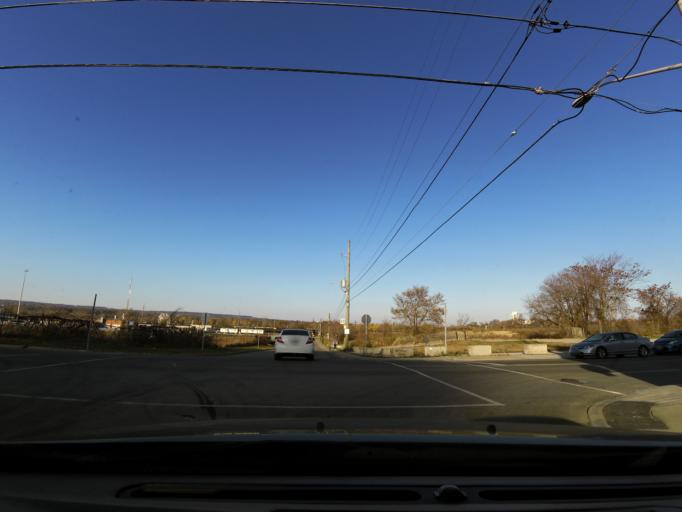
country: CA
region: Ontario
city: Hamilton
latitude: 43.2661
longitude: -79.8742
